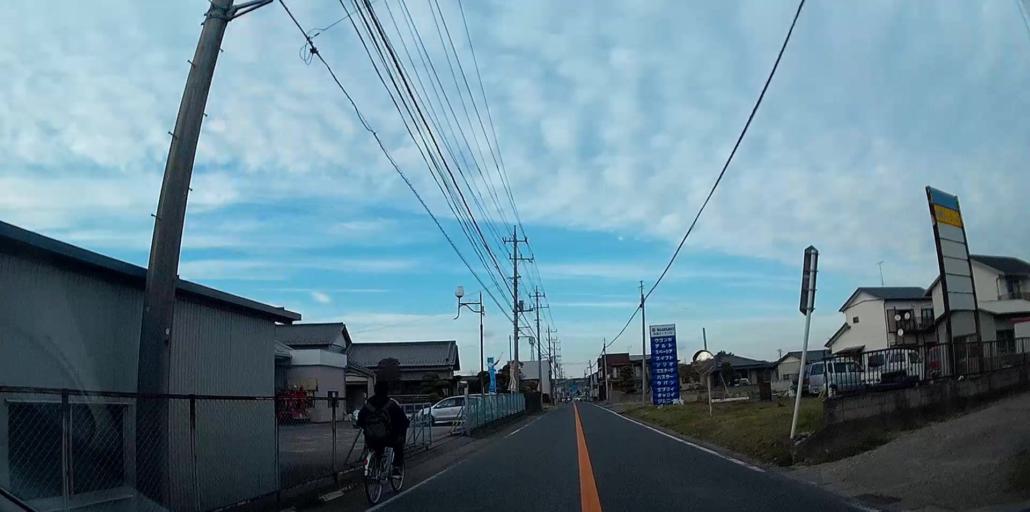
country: JP
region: Chiba
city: Kisarazu
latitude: 35.3615
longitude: 140.0578
